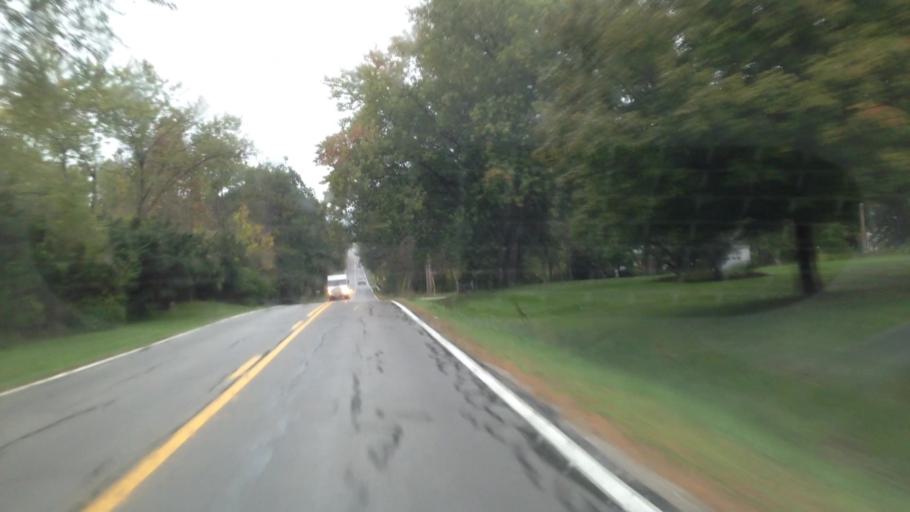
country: US
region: Ohio
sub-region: Summit County
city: Hudson
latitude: 41.2642
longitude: -81.4461
